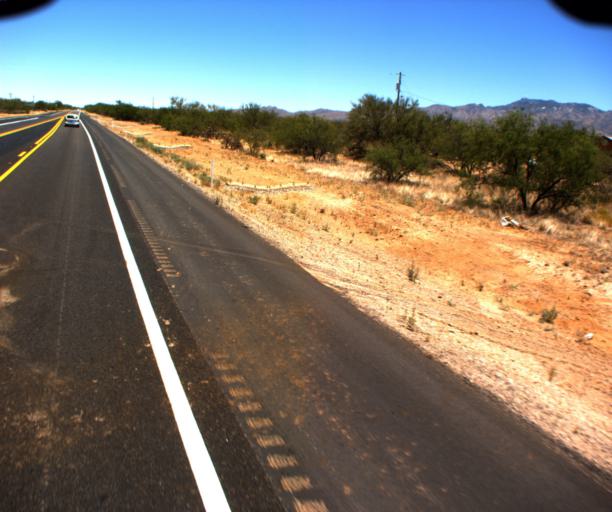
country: US
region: Arizona
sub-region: Pima County
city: Sells
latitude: 31.9348
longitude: -111.7768
